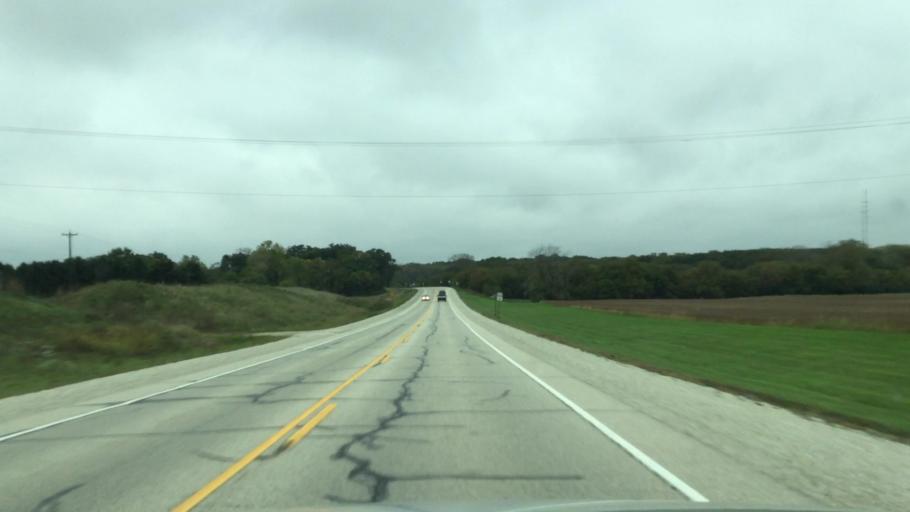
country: US
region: Wisconsin
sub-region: Racine County
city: Eagle Lake
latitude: 42.7421
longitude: -88.1401
